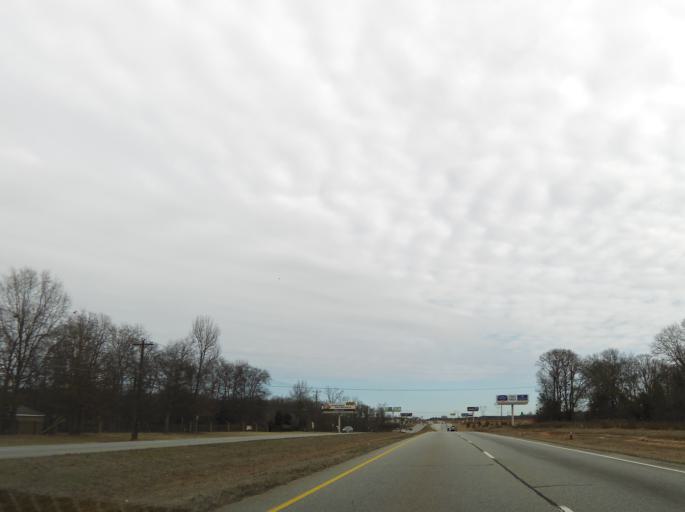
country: US
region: Georgia
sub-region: Houston County
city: Centerville
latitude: 32.6149
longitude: -83.7306
